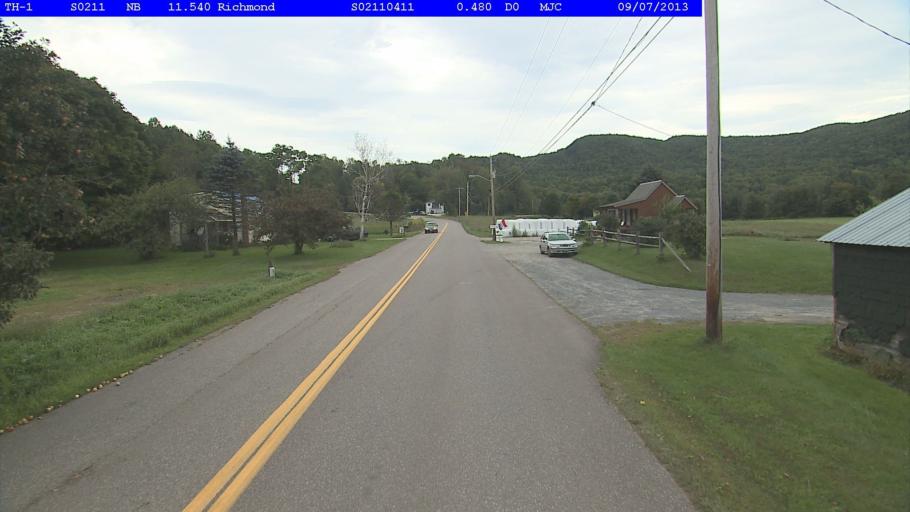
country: US
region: Vermont
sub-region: Chittenden County
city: Williston
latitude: 44.3601
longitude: -72.9933
